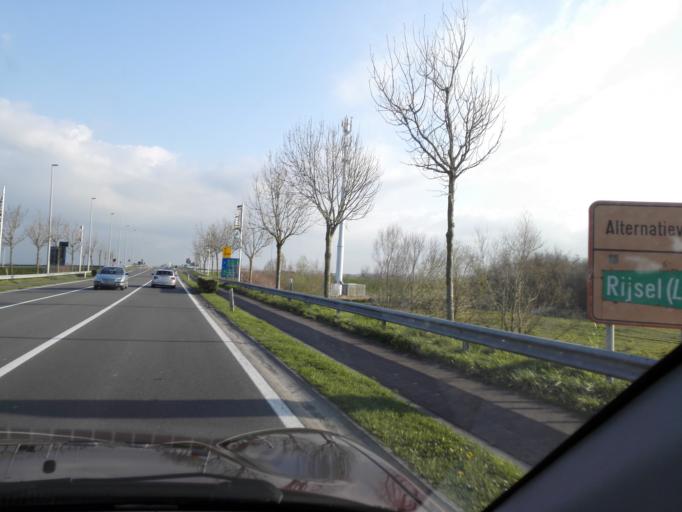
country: BE
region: Flanders
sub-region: Provincie West-Vlaanderen
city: De Panne
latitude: 51.0704
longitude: 2.6033
